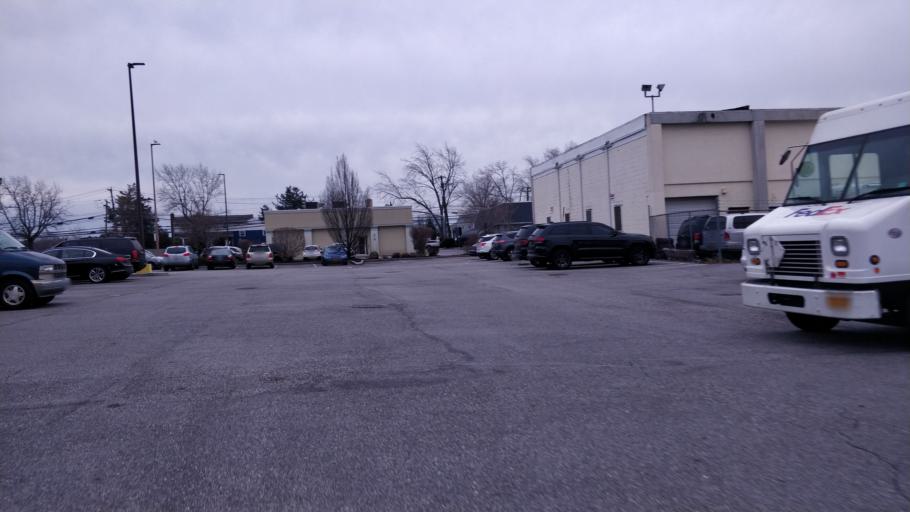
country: US
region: New York
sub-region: Nassau County
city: Salisbury
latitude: 40.7564
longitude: -73.5571
